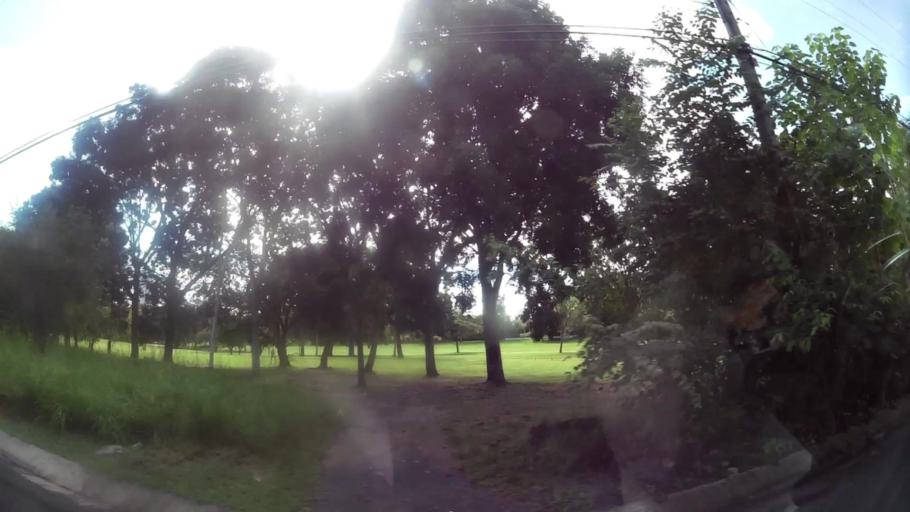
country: PA
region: Panama
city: Nueva Gorgona
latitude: 8.5392
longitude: -79.8931
